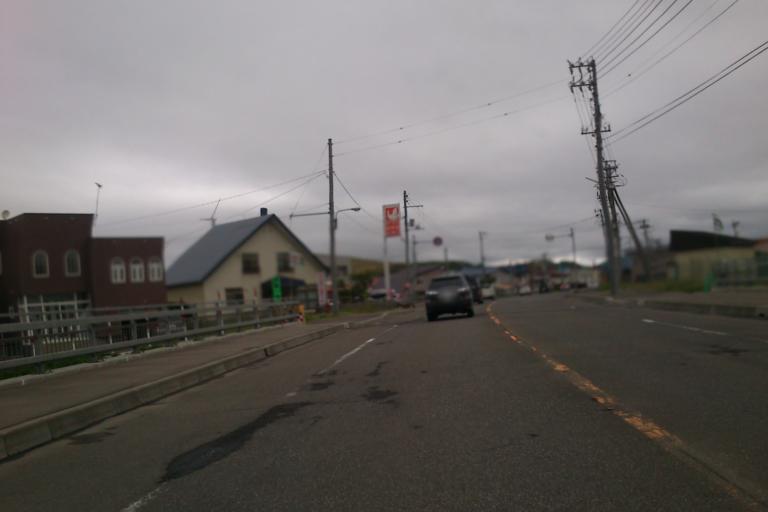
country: JP
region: Hokkaido
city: Ishikari
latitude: 43.3152
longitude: 141.4161
